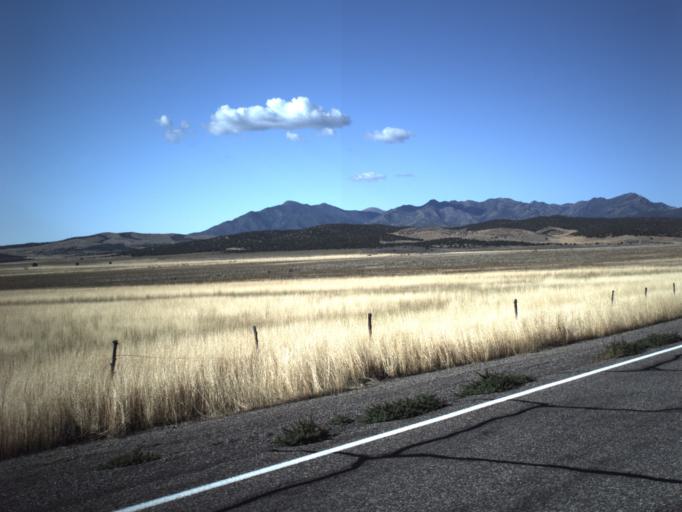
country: US
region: Utah
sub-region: Millard County
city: Fillmore
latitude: 39.1313
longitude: -112.2496
